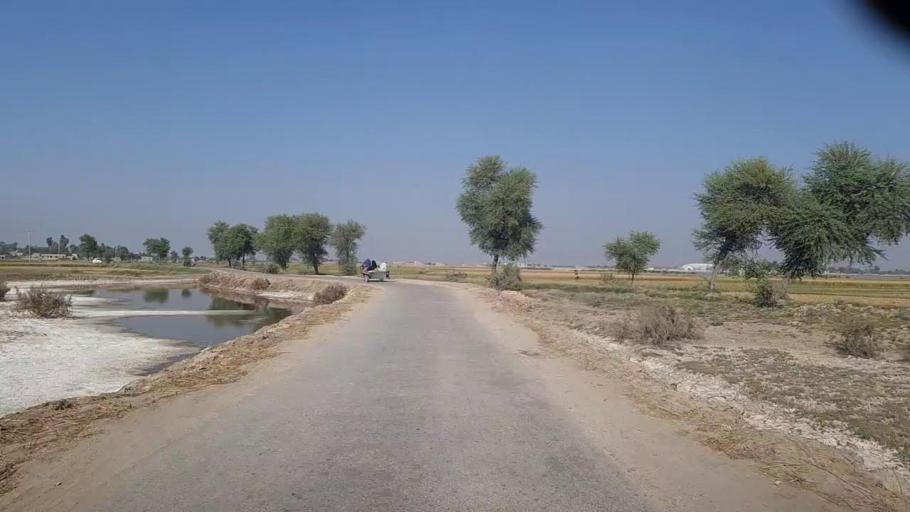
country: PK
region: Sindh
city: Tangwani
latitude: 28.2495
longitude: 68.9959
